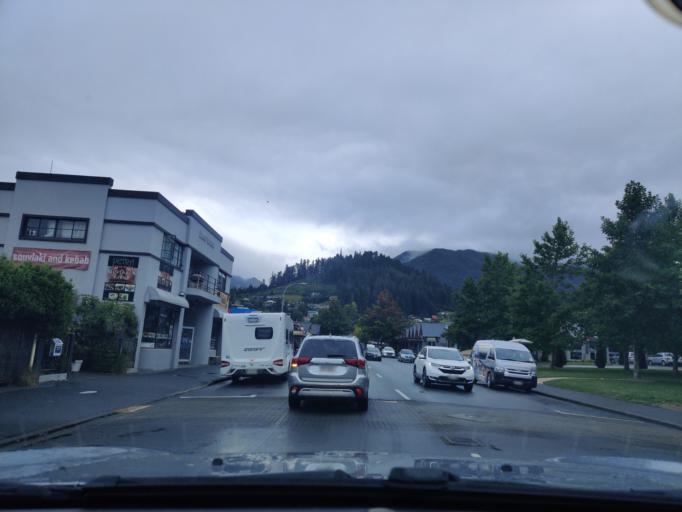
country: NZ
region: Canterbury
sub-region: Hurunui District
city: Amberley
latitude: -42.5211
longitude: 172.8296
